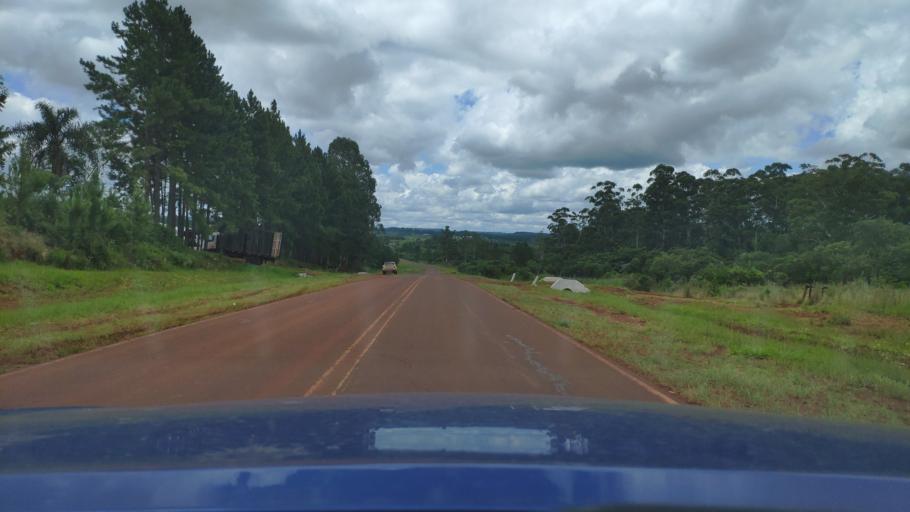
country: AR
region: Misiones
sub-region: Departamento de San Javier
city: San Javier
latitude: -27.8544
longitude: -55.2495
